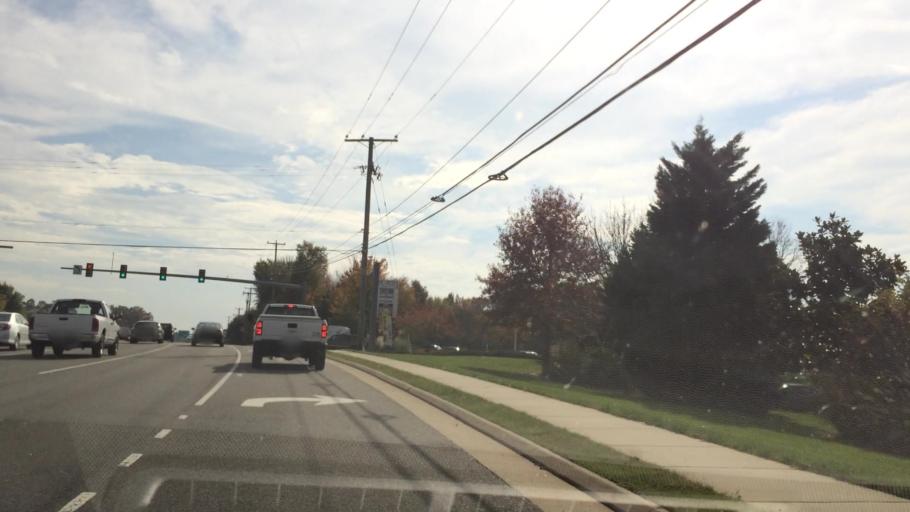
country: US
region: Virginia
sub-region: Henrico County
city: Glen Allen
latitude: 37.6692
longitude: -77.4612
